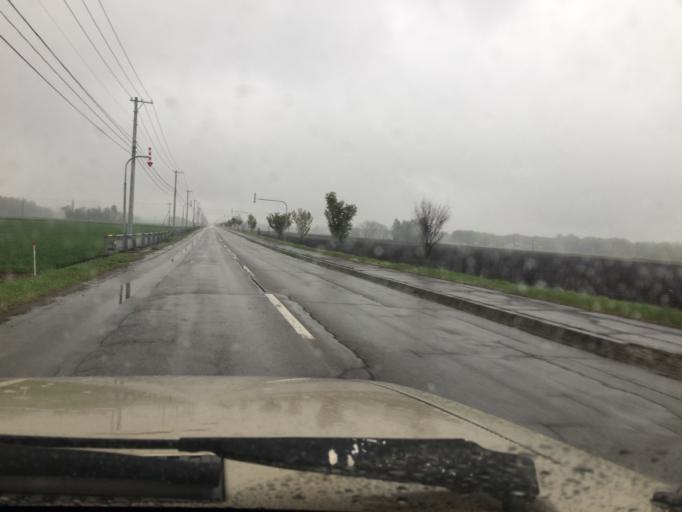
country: JP
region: Hokkaido
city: Obihiro
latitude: 42.8793
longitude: 143.0306
